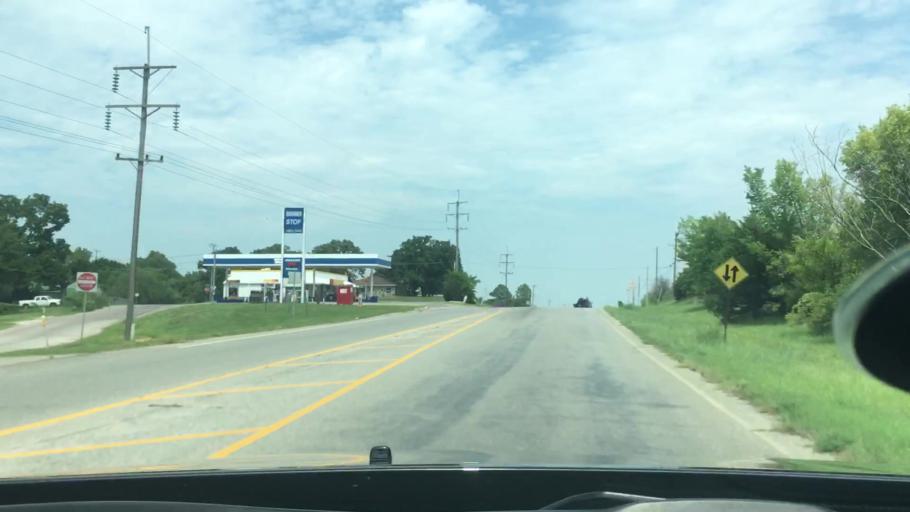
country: US
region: Oklahoma
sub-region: Pontotoc County
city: Ada
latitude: 34.8167
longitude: -96.6786
